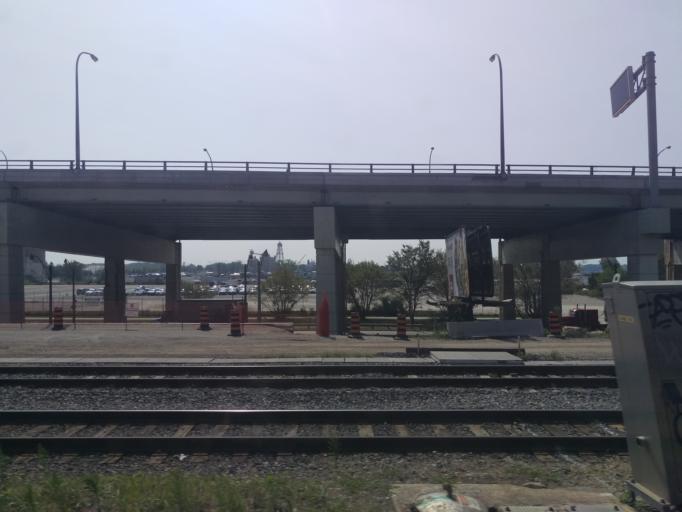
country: CA
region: Ontario
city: Toronto
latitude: 43.6492
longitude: -79.3587
